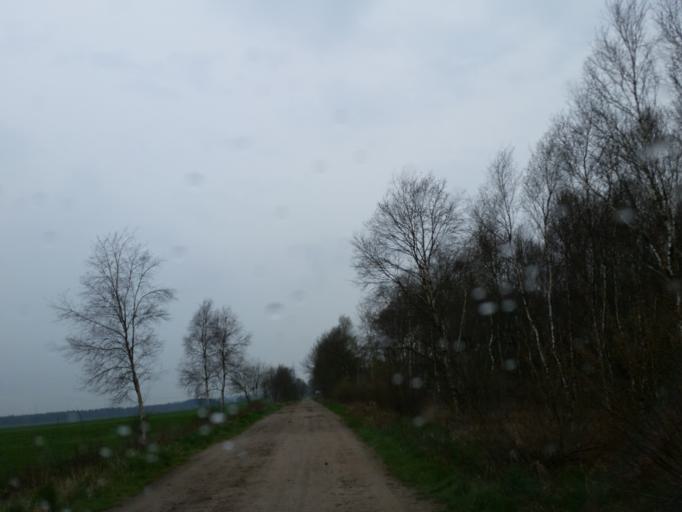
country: DE
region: Lower Saxony
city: Alfstedt
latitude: 53.5625
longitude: 9.0099
